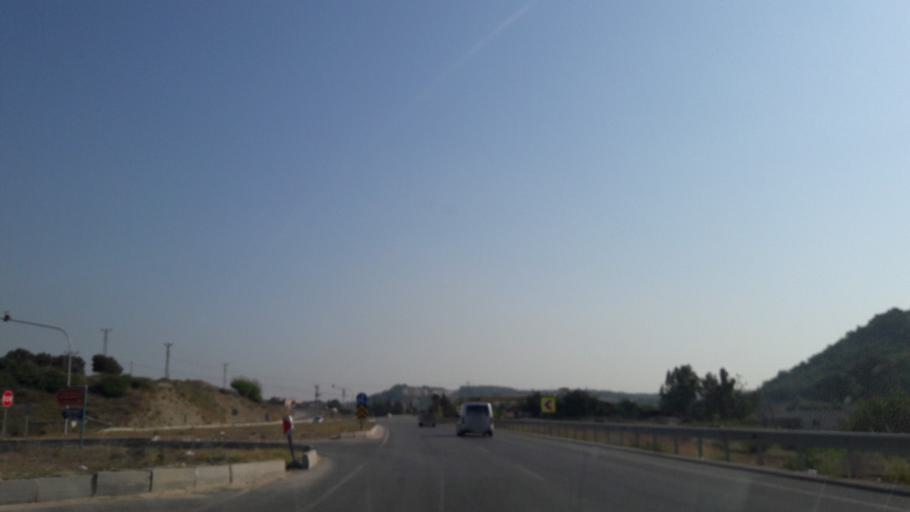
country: TR
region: Adana
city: Yuregir
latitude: 37.0701
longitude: 35.4566
